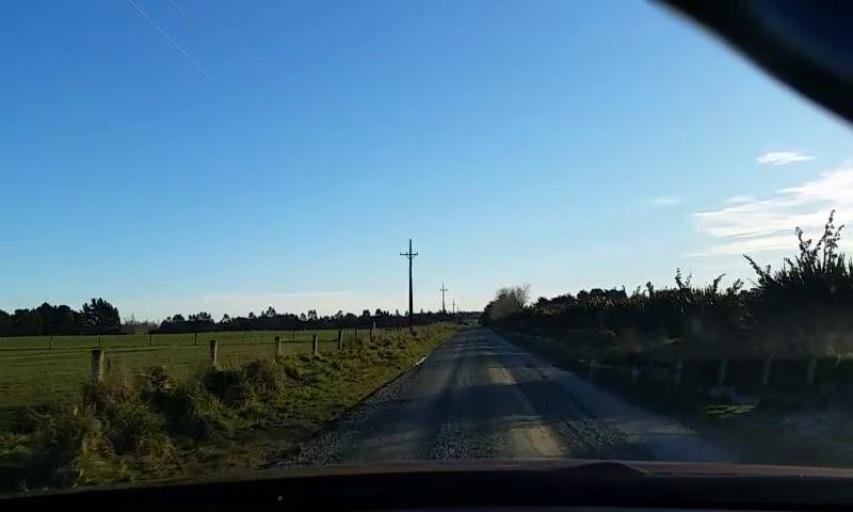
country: NZ
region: Southland
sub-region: Invercargill City
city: Invercargill
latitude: -46.2916
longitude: 168.4253
